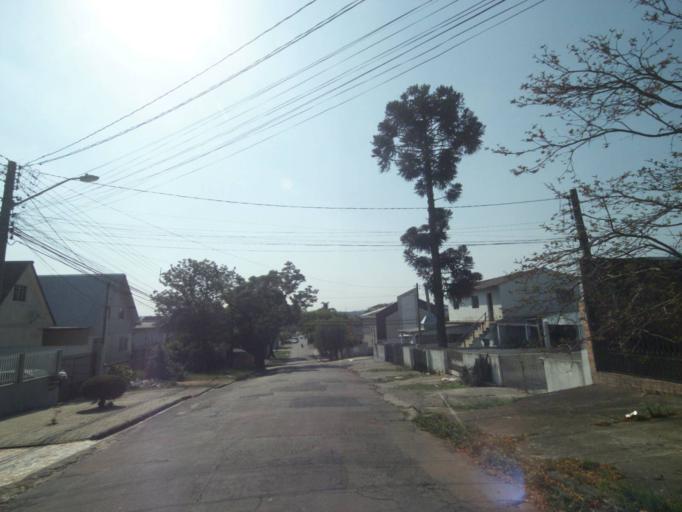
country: BR
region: Parana
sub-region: Curitiba
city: Curitiba
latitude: -25.4822
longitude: -49.3272
